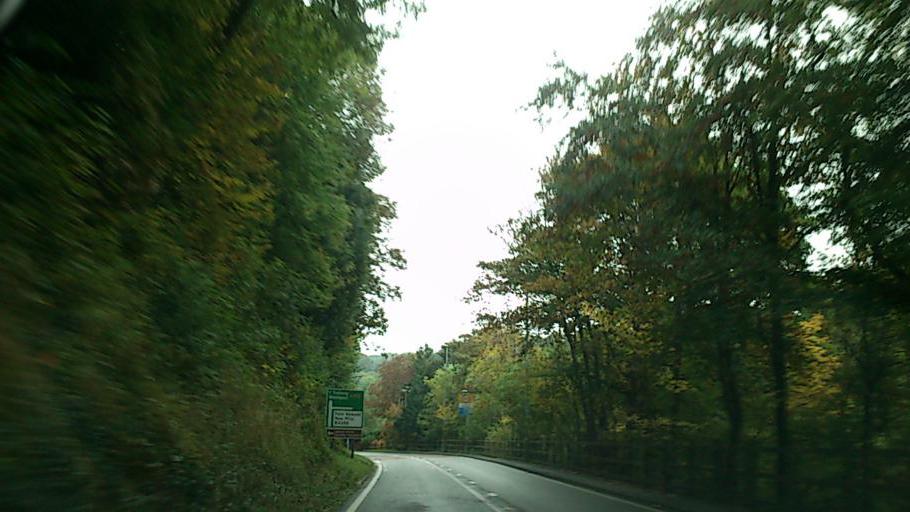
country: GB
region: Wales
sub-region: Sir Powys
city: Llanfyllin
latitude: 52.6498
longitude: -3.3310
